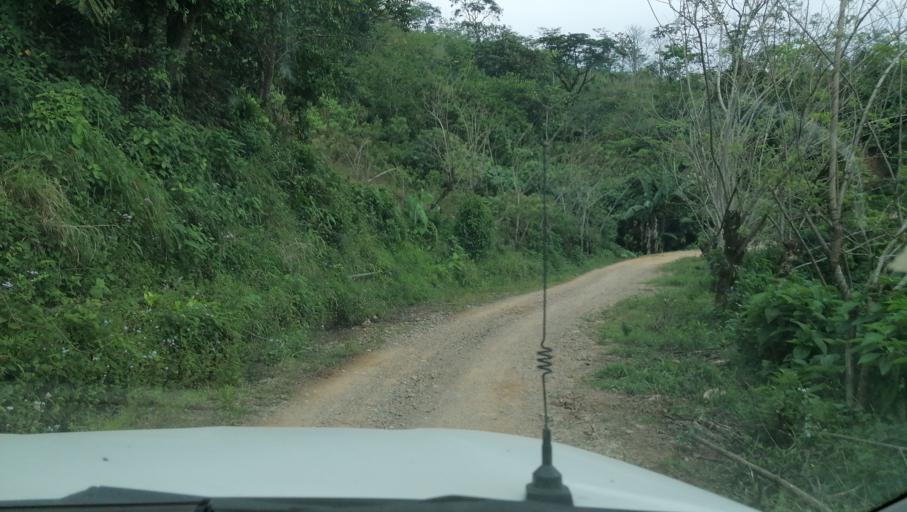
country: MX
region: Chiapas
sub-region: Francisco Leon
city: San Miguel la Sardina
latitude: 17.3364
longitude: -93.3134
